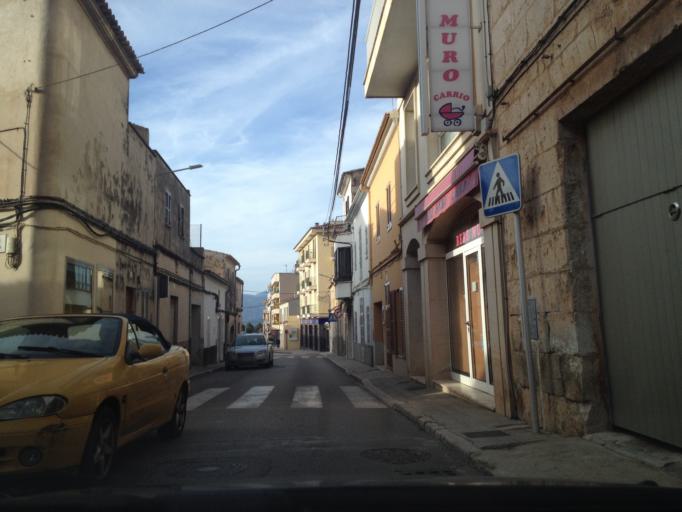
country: ES
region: Balearic Islands
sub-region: Illes Balears
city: Muro
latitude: 39.7374
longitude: 3.0551
